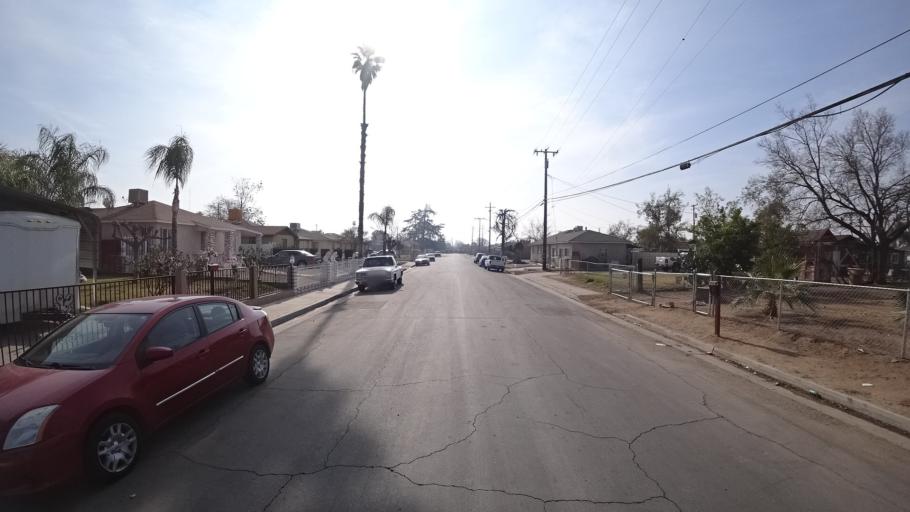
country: US
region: California
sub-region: Kern County
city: Bakersfield
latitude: 35.3519
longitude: -119.0140
